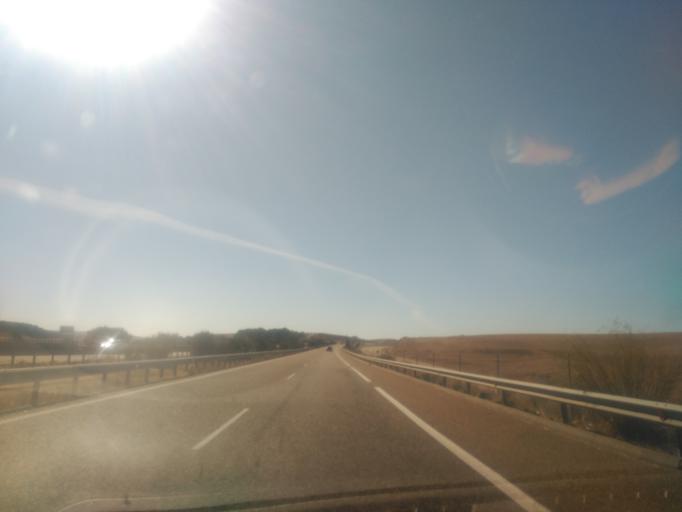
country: ES
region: Castille and Leon
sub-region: Provincia de Valladolid
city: Pollos
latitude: 41.4477
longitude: -5.0894
